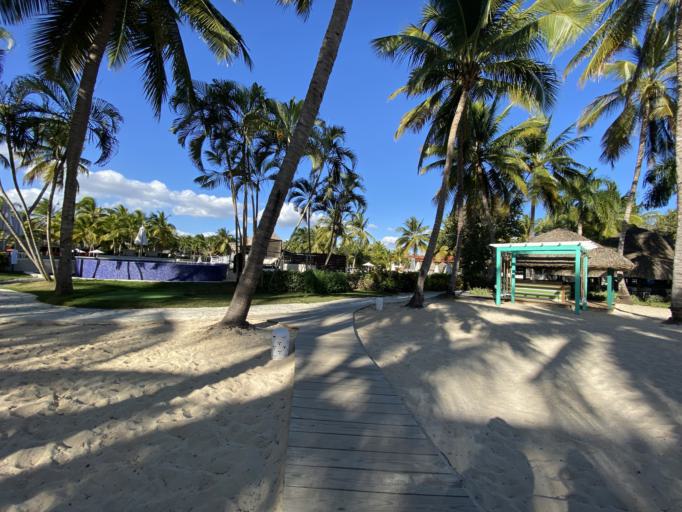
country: DO
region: La Romana
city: La Romana
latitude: 18.3433
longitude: -68.8227
